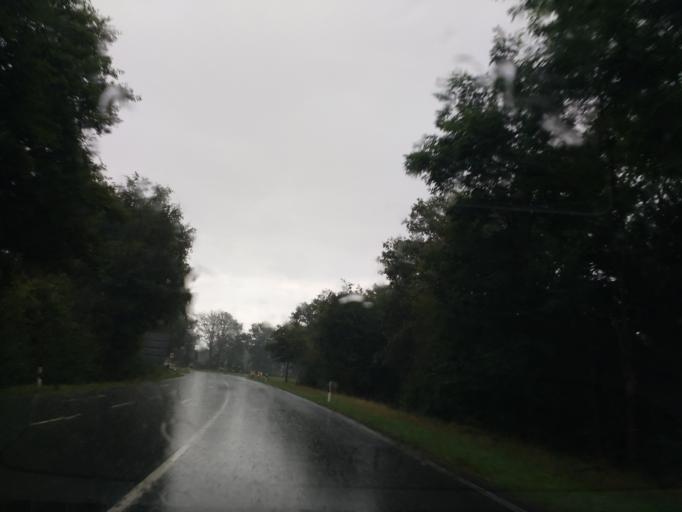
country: DE
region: North Rhine-Westphalia
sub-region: Regierungsbezirk Munster
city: Ostbevern
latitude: 52.1142
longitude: 7.8704
